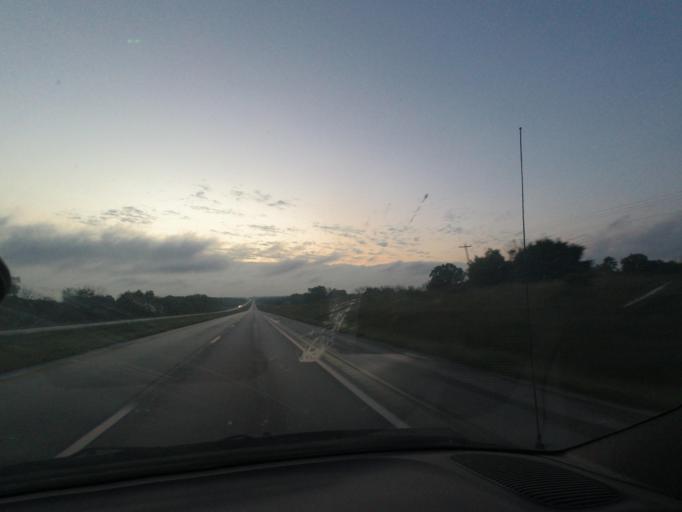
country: US
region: Missouri
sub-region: Linn County
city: Brookfield
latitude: 39.7621
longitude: -93.0043
